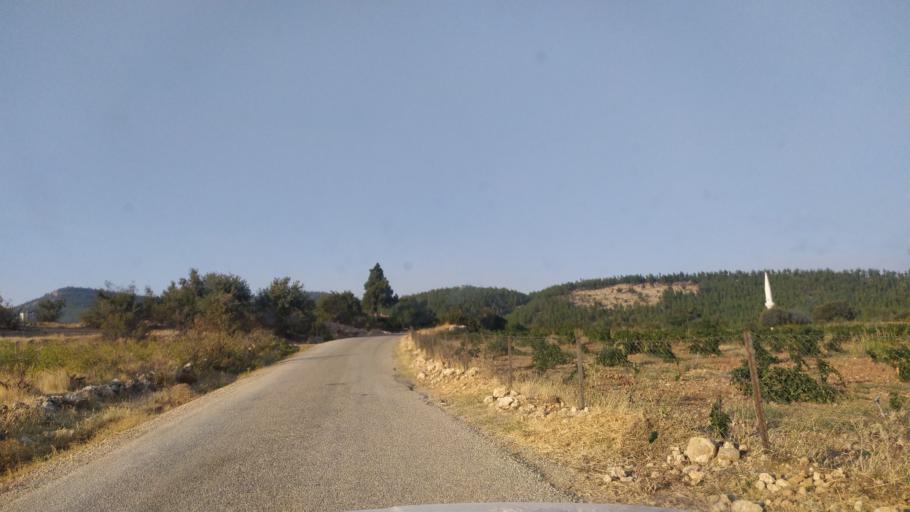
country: TR
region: Mersin
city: Mut
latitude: 36.6910
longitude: 33.1986
